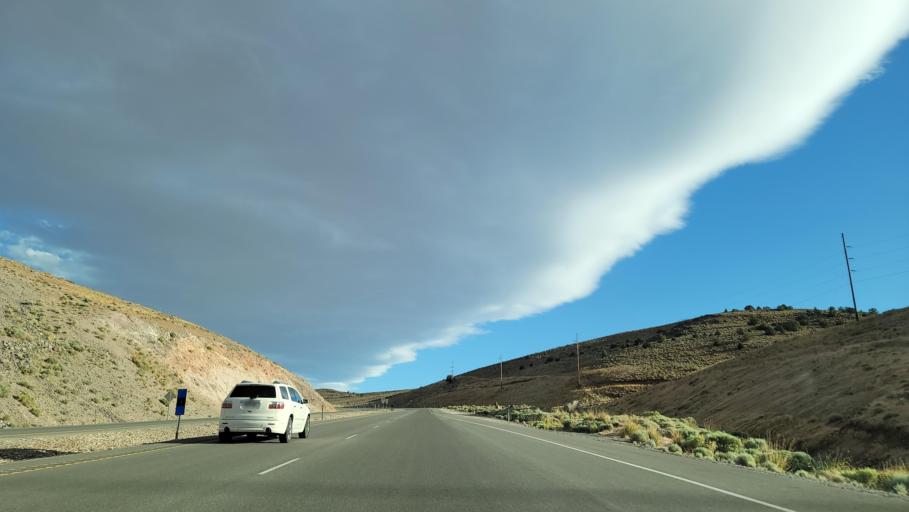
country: US
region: Nevada
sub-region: Lyon County
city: Stagecoach
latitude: 39.4854
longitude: -119.4015
